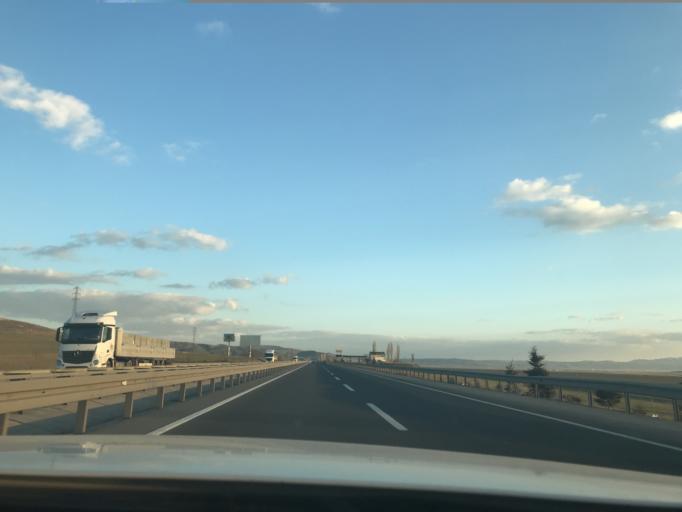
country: TR
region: Ankara
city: Altpinar
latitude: 39.3863
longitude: 32.8889
